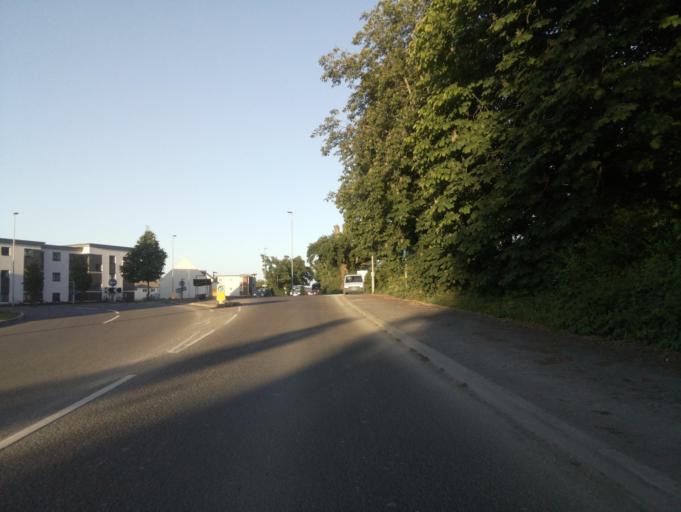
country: GB
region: England
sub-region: Devon
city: Newton Abbot
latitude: 50.5367
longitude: -3.6480
